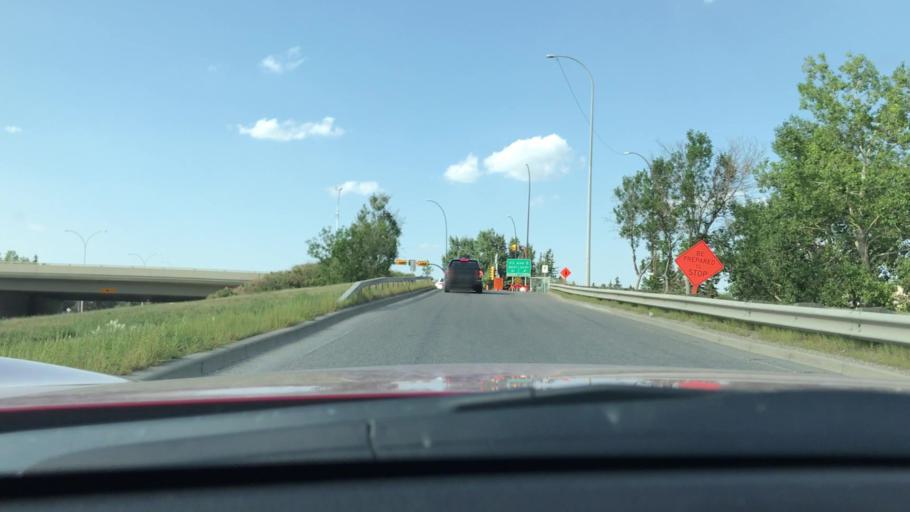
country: CA
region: Alberta
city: Calgary
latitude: 51.0231
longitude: -114.1176
